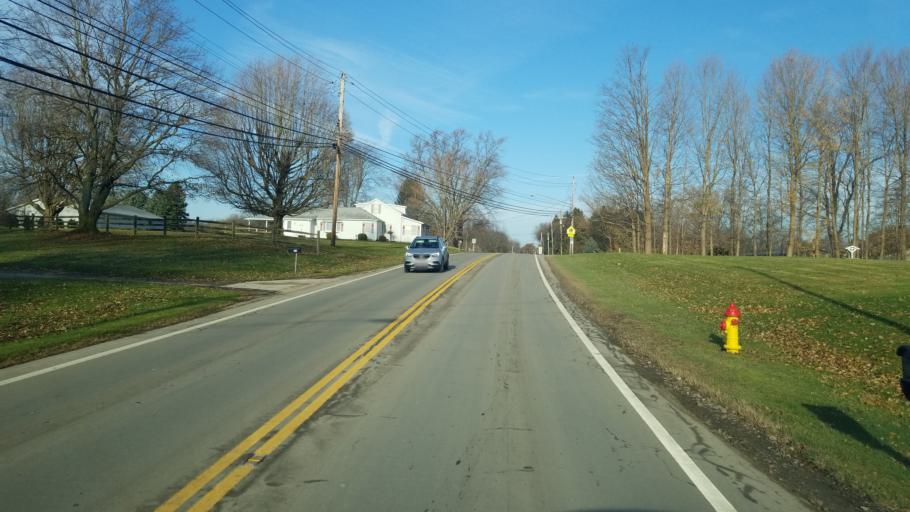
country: US
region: Ohio
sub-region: Ashtabula County
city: North Kingsville
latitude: 41.8852
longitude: -80.6702
